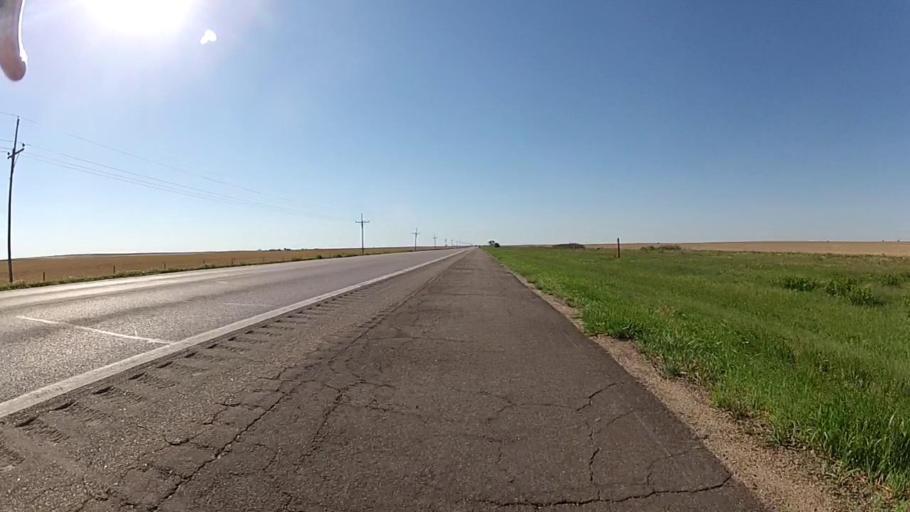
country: US
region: Kansas
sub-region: Ford County
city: Dodge City
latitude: 37.5999
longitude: -99.7004
